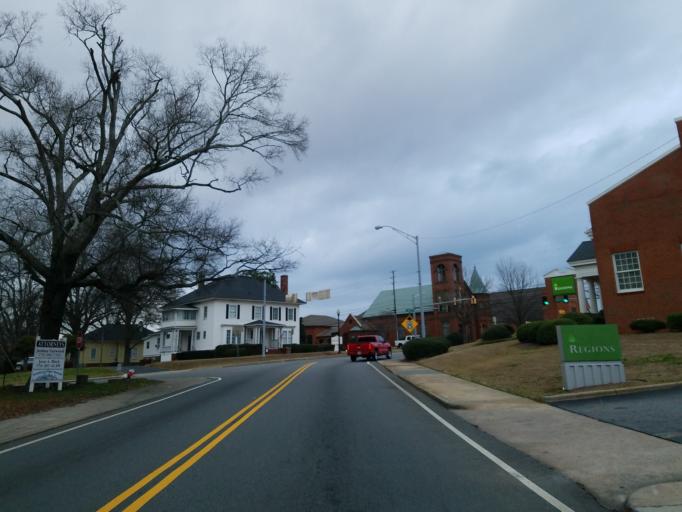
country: US
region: Georgia
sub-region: Bartow County
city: Cartersville
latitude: 34.1634
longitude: -84.8007
